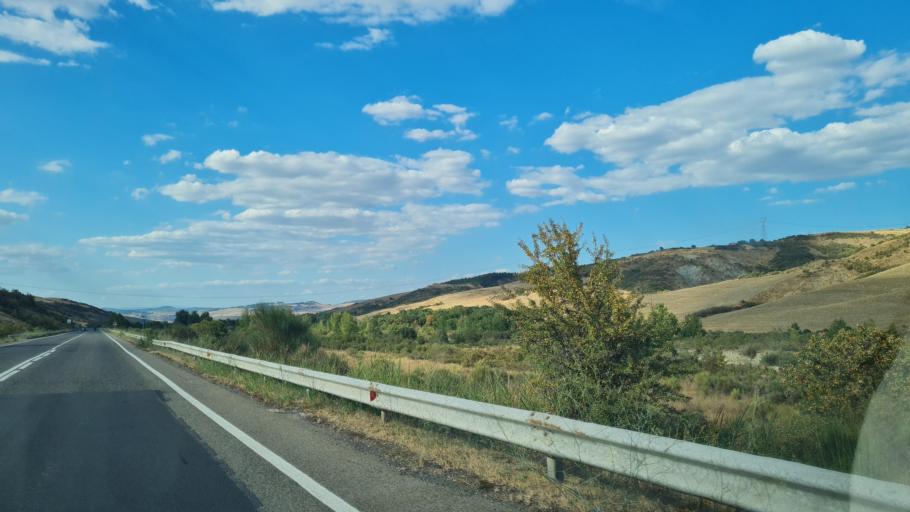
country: IT
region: Tuscany
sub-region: Provincia di Siena
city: Abbadia San Salvatore
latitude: 42.9523
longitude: 11.7075
